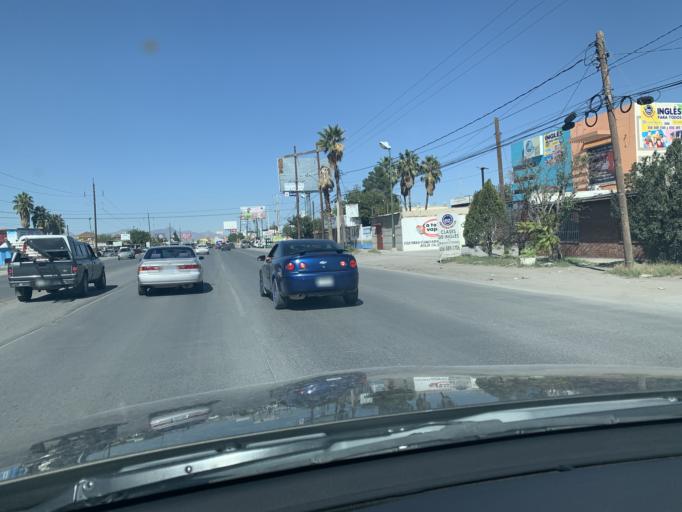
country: US
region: Texas
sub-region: El Paso County
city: Socorro
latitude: 31.6793
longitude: -106.3708
